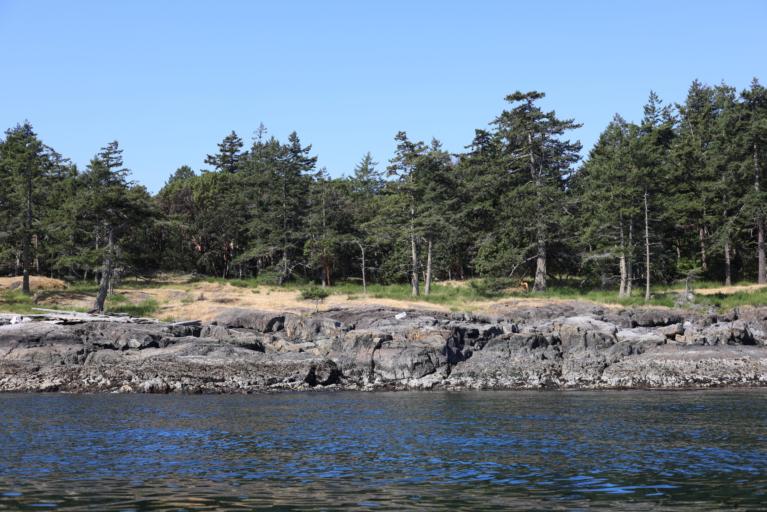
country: CA
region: British Columbia
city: Colwood
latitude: 48.3893
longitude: -123.4767
